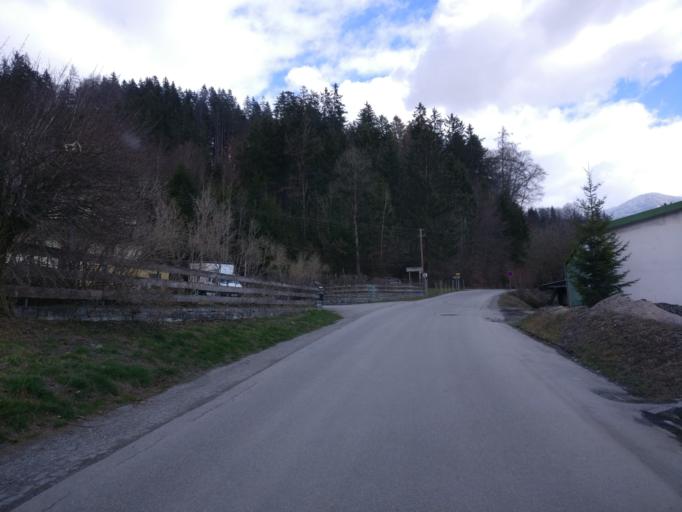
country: AT
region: Salzburg
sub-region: Politischer Bezirk Sankt Johann im Pongau
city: Bischofshofen
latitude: 47.4379
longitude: 13.2149
